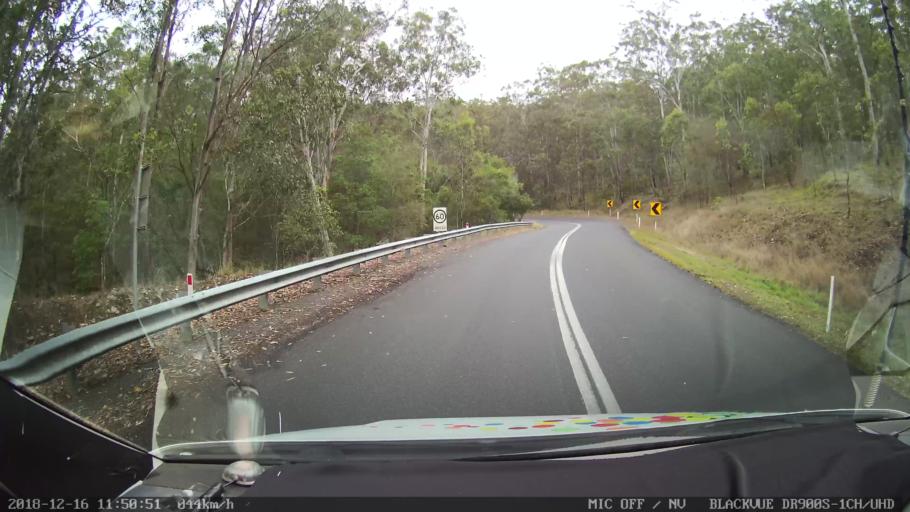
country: AU
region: New South Wales
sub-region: Tenterfield Municipality
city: Carrolls Creek
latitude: -28.9060
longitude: 152.2633
